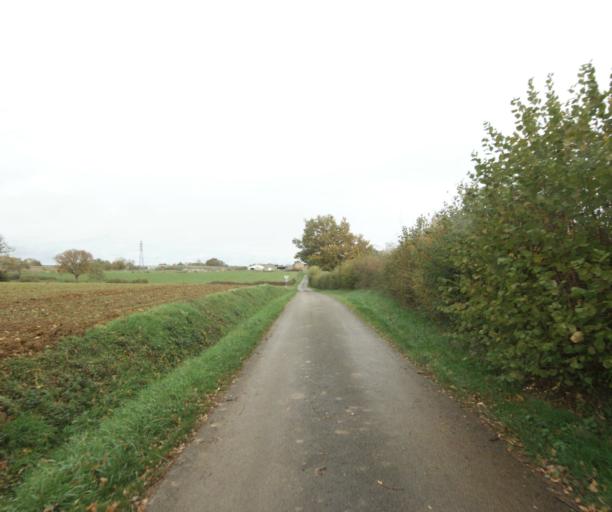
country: FR
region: Rhone-Alpes
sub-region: Departement de l'Ain
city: Pont-de-Vaux
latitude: 46.4605
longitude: 4.8797
